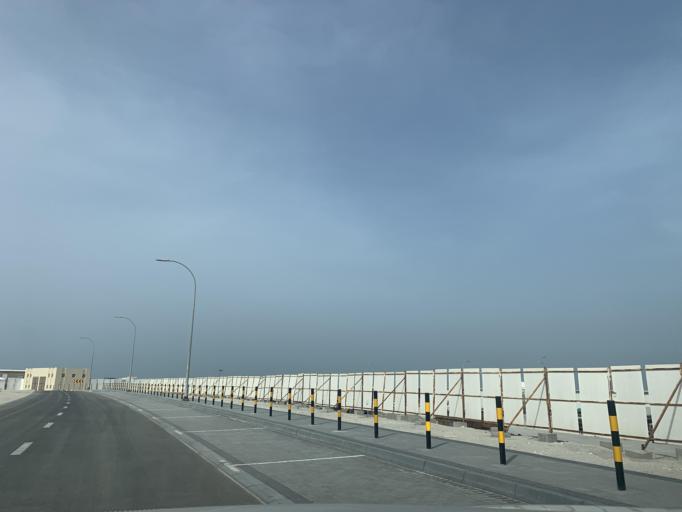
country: BH
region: Muharraq
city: Al Muharraq
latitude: 26.3219
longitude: 50.6306
